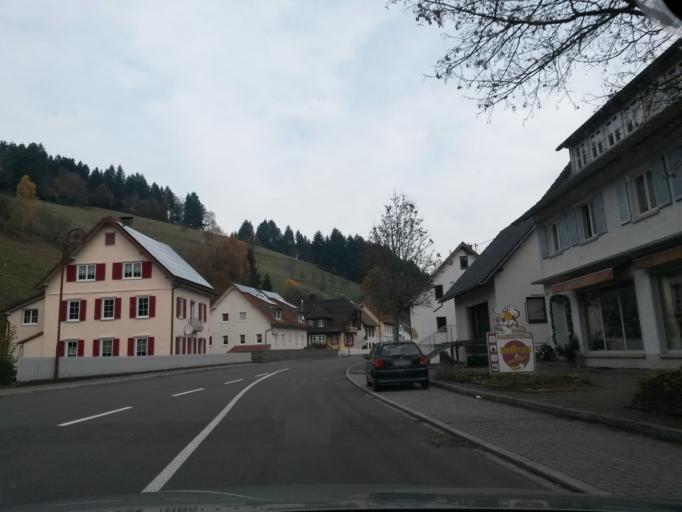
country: DE
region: Baden-Wuerttemberg
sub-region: Freiburg Region
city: Schenkenzell
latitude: 48.3116
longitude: 8.3730
